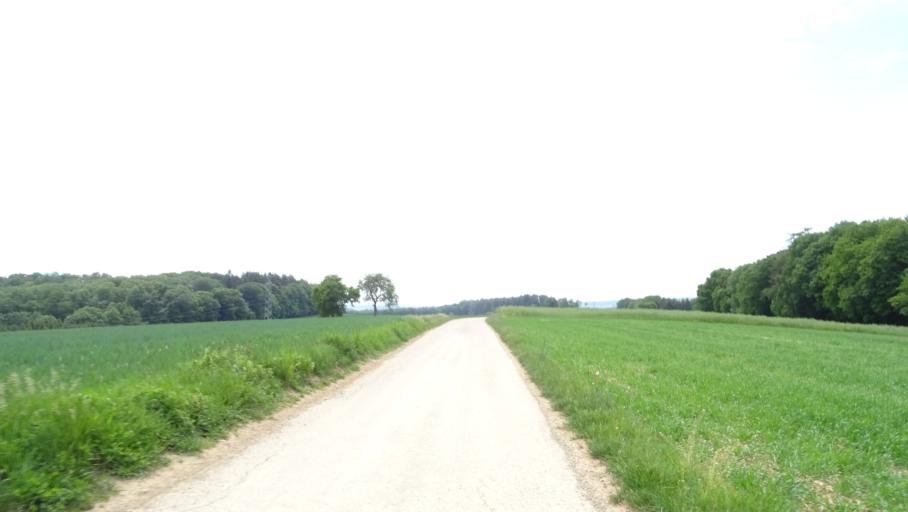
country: DE
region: Baden-Wuerttemberg
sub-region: Karlsruhe Region
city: Binau
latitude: 49.3783
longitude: 9.0544
